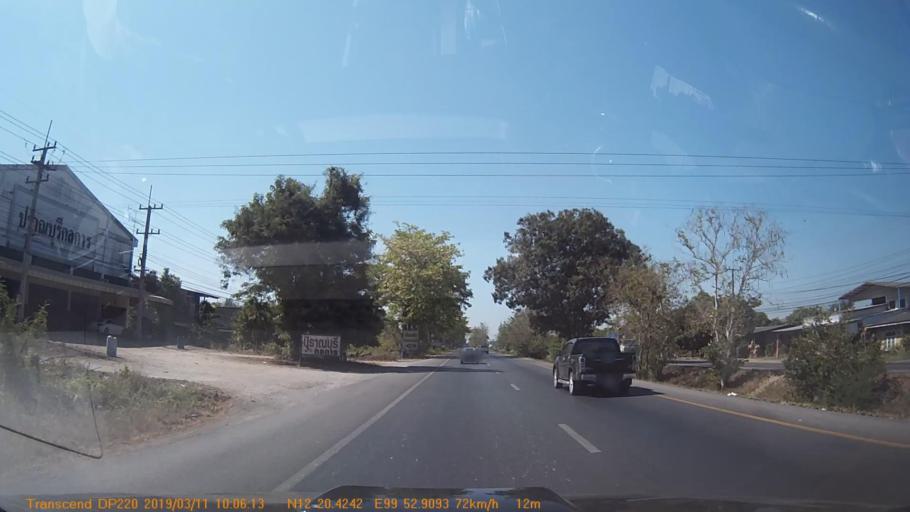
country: TH
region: Prachuap Khiri Khan
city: Pran Buri
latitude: 12.3399
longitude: 99.8817
